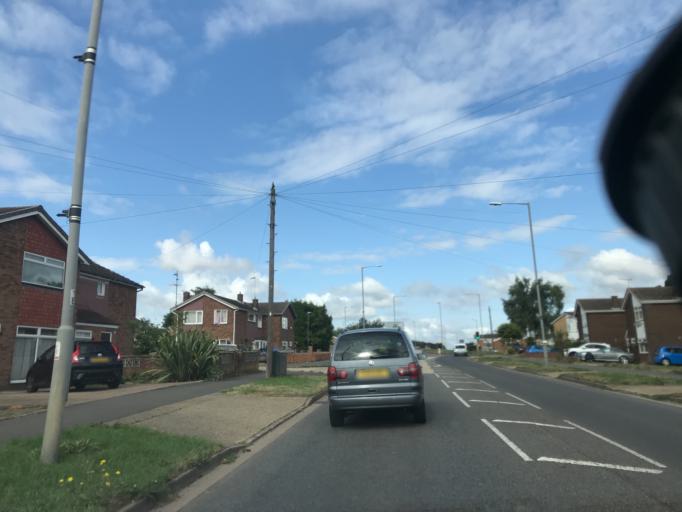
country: GB
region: England
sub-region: Buckinghamshire
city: Aylesbury
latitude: 51.8232
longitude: -0.7973
